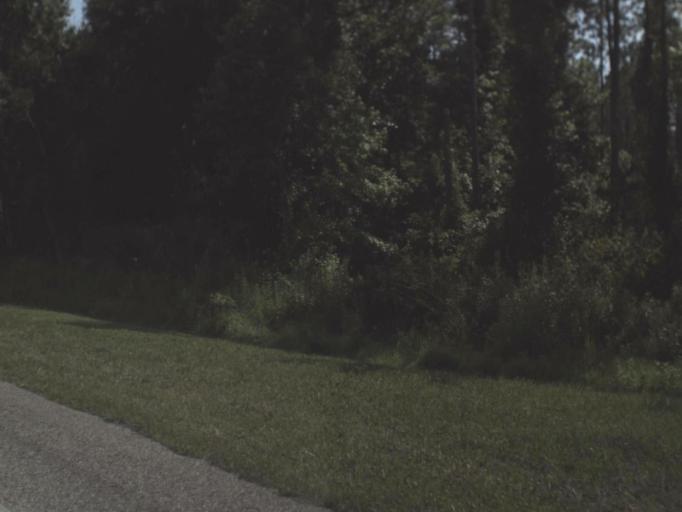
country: US
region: Florida
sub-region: Marion County
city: Citra
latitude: 29.4909
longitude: -82.1009
